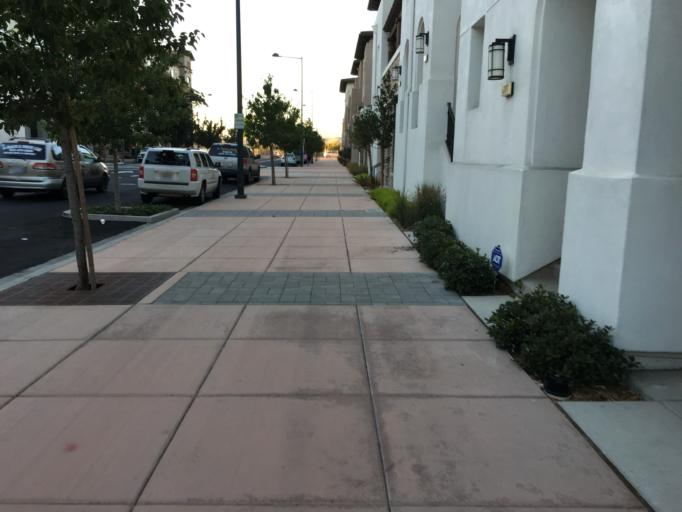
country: US
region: California
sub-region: Alameda County
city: Dublin
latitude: 37.7047
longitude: -121.8971
